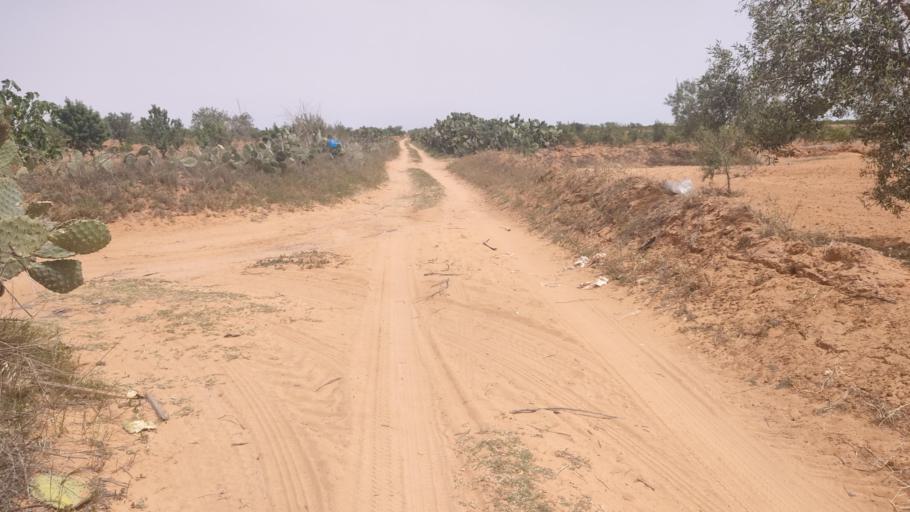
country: TN
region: Safaqis
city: Sfax
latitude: 34.8467
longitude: 10.5956
